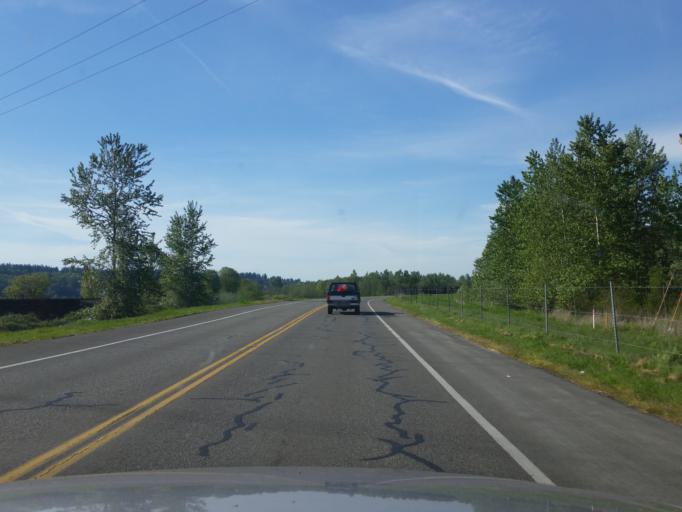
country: US
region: Washington
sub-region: Snohomish County
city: Fobes Hill
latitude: 47.9280
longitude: -122.1698
